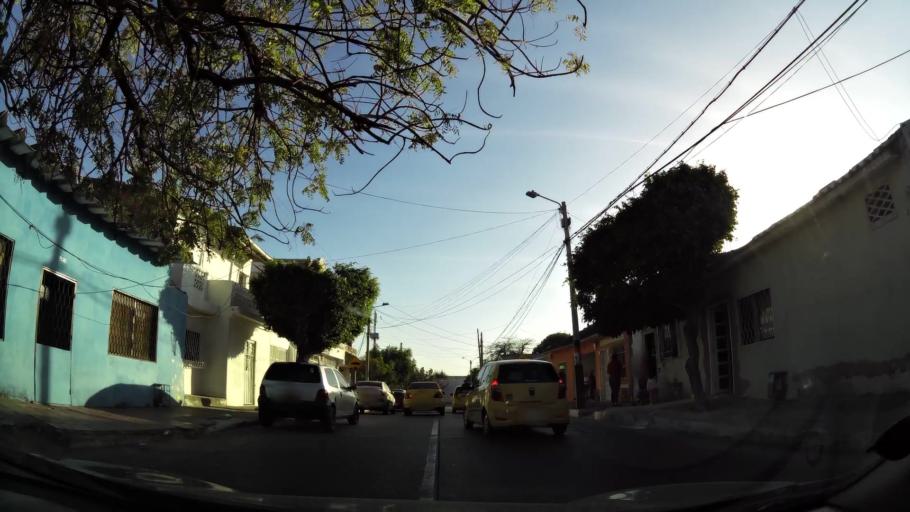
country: CO
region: Atlantico
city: Barranquilla
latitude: 10.9763
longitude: -74.7926
